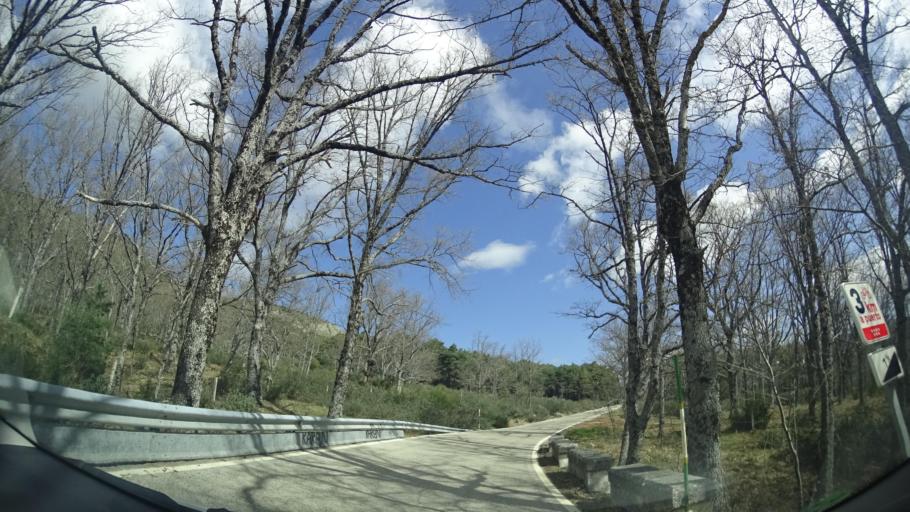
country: ES
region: Madrid
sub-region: Provincia de Madrid
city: Miraflores de la Sierra
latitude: 40.8447
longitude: -3.7652
